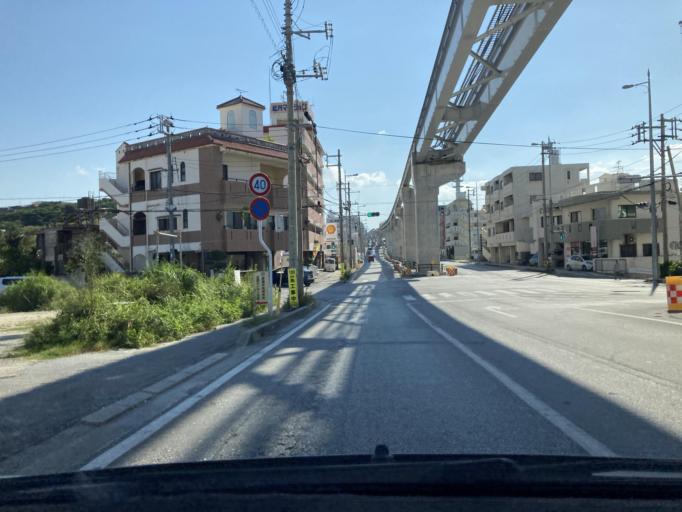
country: JP
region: Okinawa
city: Ginowan
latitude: 26.2263
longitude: 127.7289
